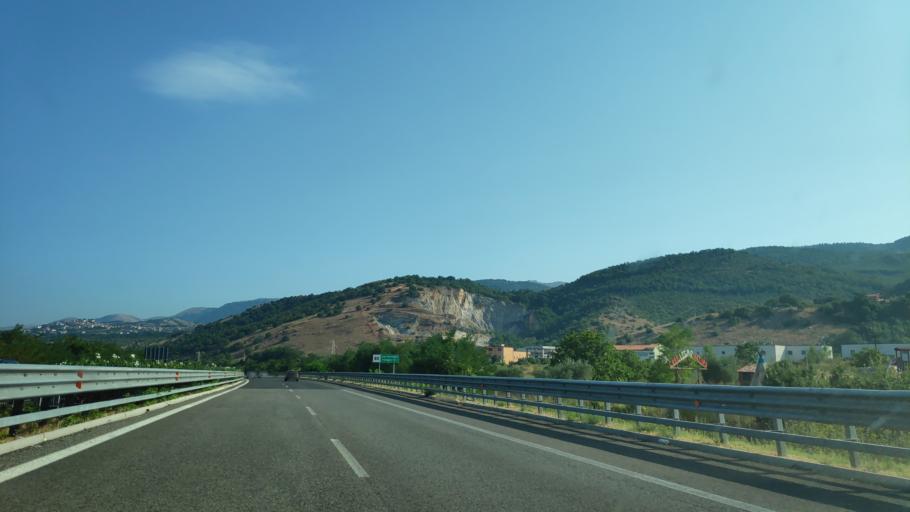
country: IT
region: Campania
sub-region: Provincia di Salerno
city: Atena Lucana
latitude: 40.4263
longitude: 15.5591
